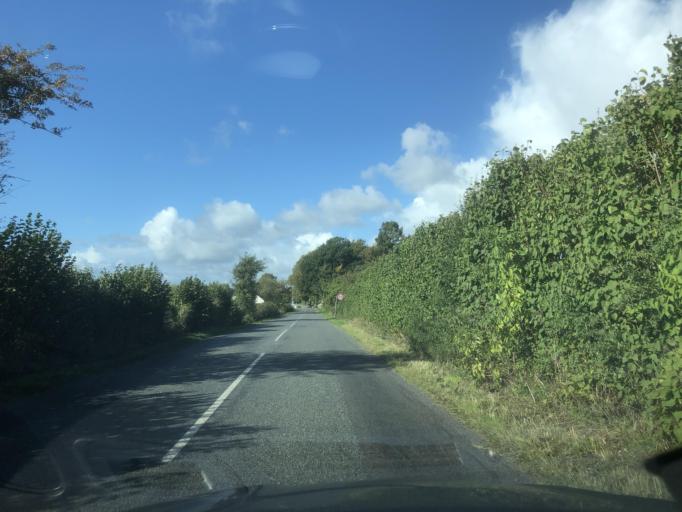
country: DK
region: South Denmark
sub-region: Faaborg-Midtfyn Kommune
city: Ringe
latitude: 55.2454
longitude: 10.3755
